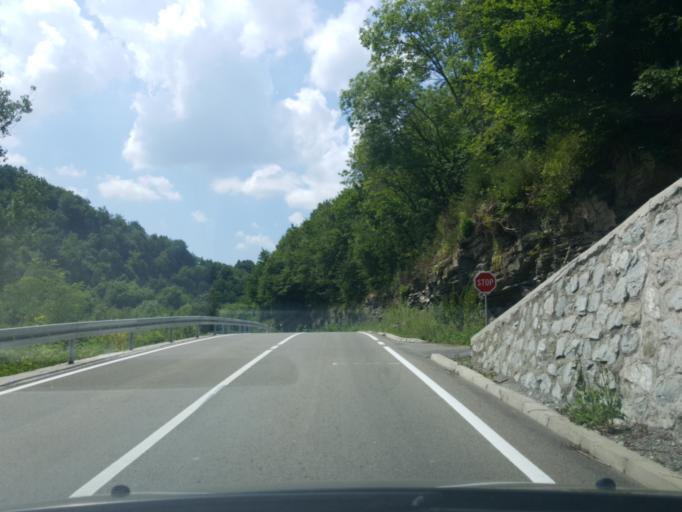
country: RS
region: Central Serbia
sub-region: Moravicki Okrug
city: Gornji Milanovac
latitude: 44.1636
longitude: 20.5134
